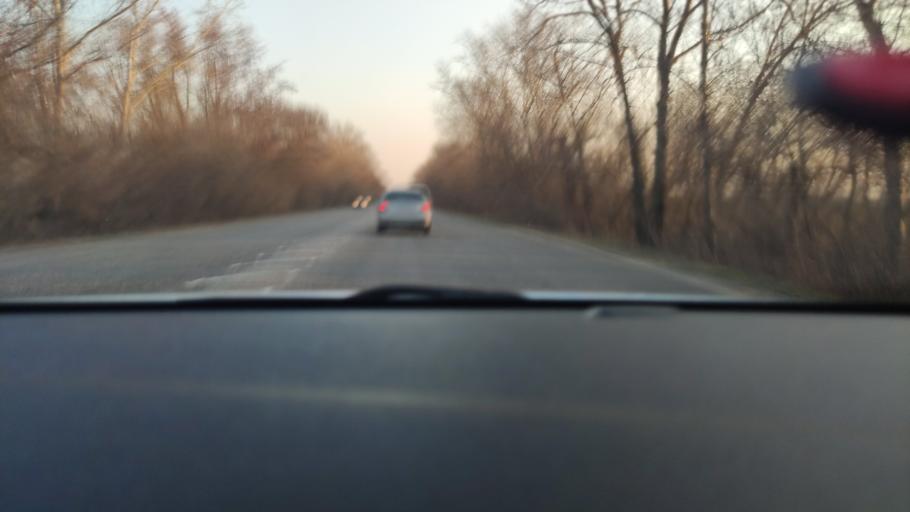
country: RU
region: Voronezj
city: Maslovka
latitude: 51.4816
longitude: 39.3070
